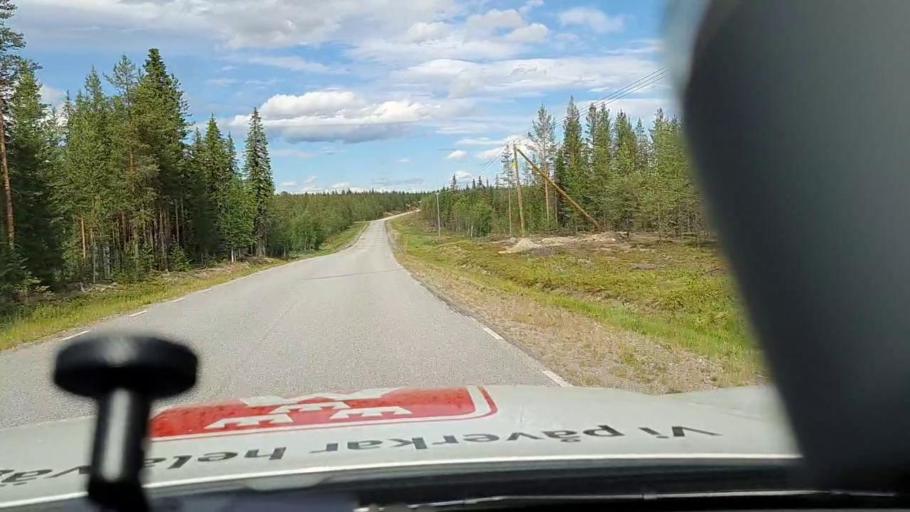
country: SE
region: Norrbotten
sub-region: Jokkmokks Kommun
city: Jokkmokk
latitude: 66.6875
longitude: 20.1692
